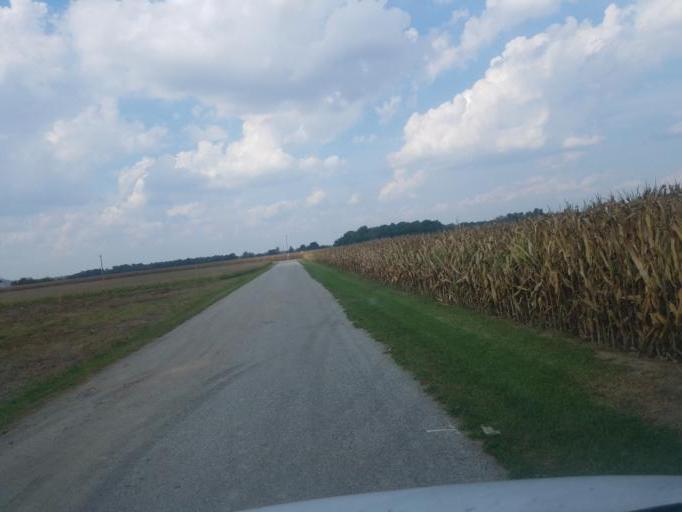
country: US
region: Ohio
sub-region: Hardin County
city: Kenton
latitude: 40.7298
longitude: -83.6145
